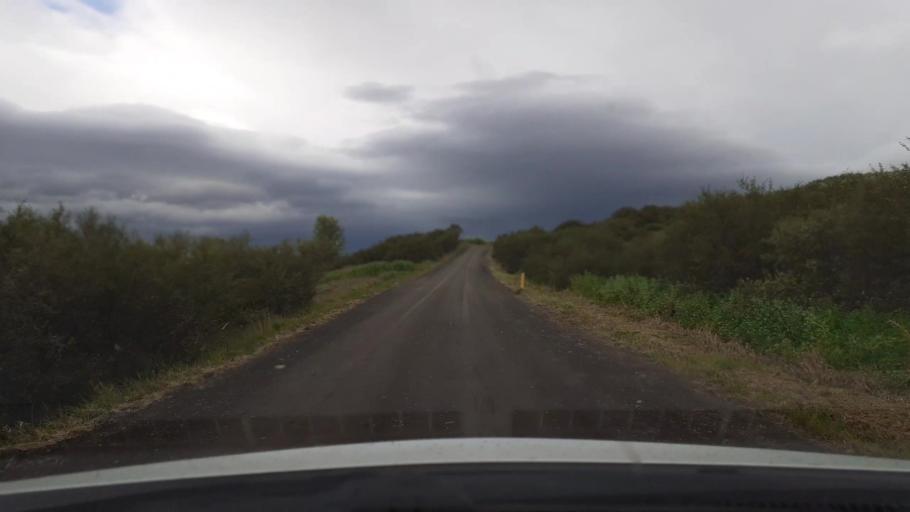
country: IS
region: Capital Region
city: Mosfellsbaer
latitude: 64.5217
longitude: -21.4642
